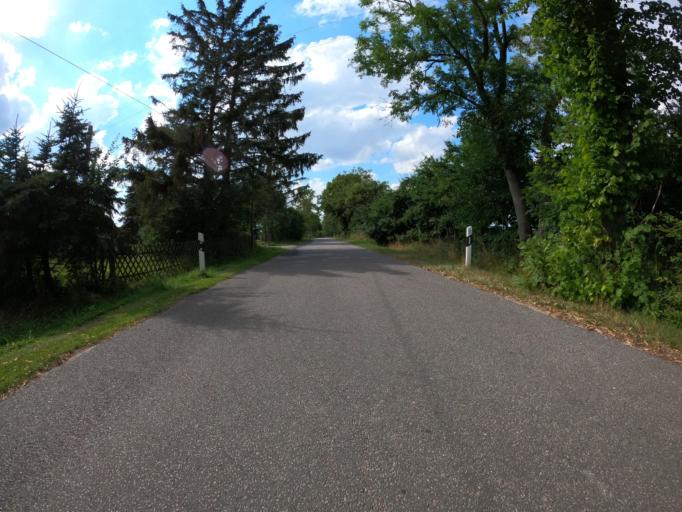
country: DE
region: Mecklenburg-Vorpommern
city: Woldegk
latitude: 53.4373
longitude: 13.5979
